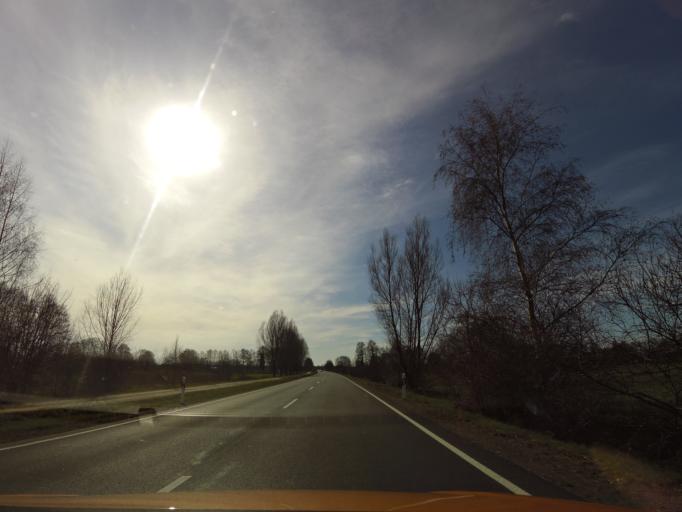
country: DE
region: Brandenburg
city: Beelitz
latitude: 52.2440
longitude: 12.9856
